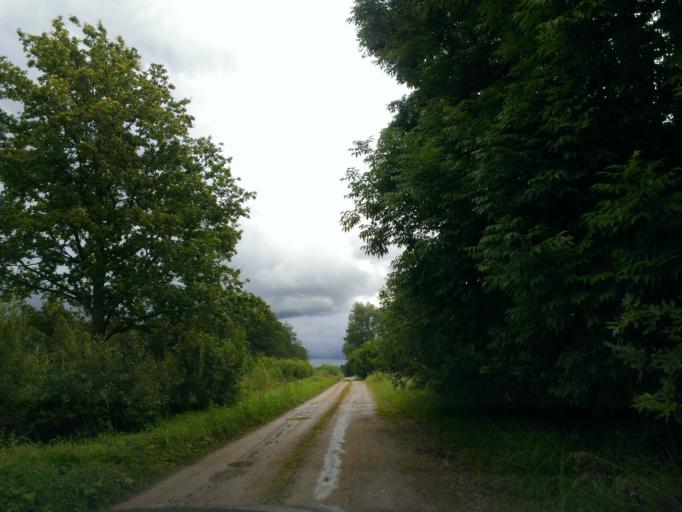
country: LV
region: Sigulda
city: Sigulda
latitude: 57.2149
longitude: 24.9390
